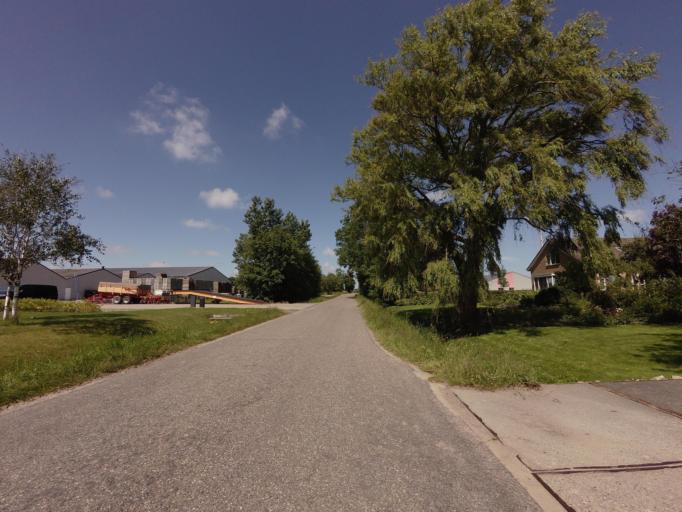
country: NL
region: North Holland
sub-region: Gemeente Schagen
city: Schagen
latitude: 52.8819
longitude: 4.8381
